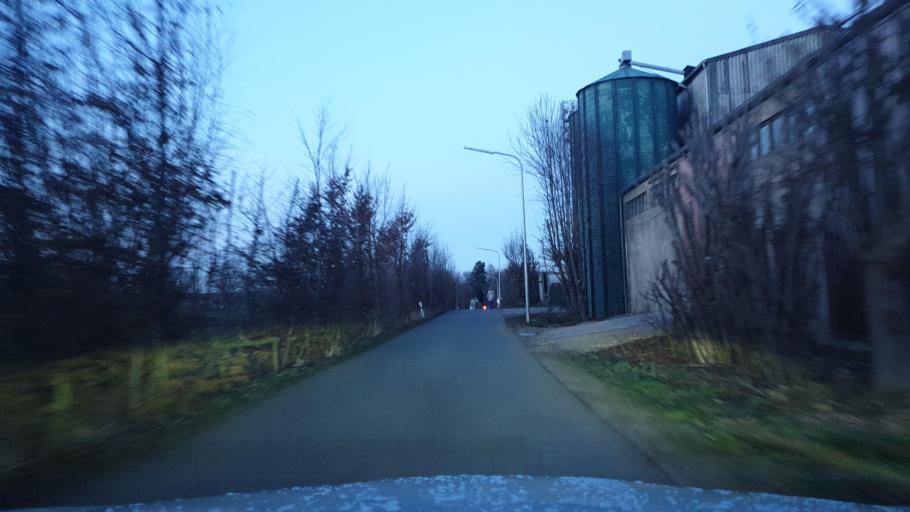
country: DE
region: North Rhine-Westphalia
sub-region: Regierungsbezirk Detmold
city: Minden
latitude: 52.2611
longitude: 8.8569
